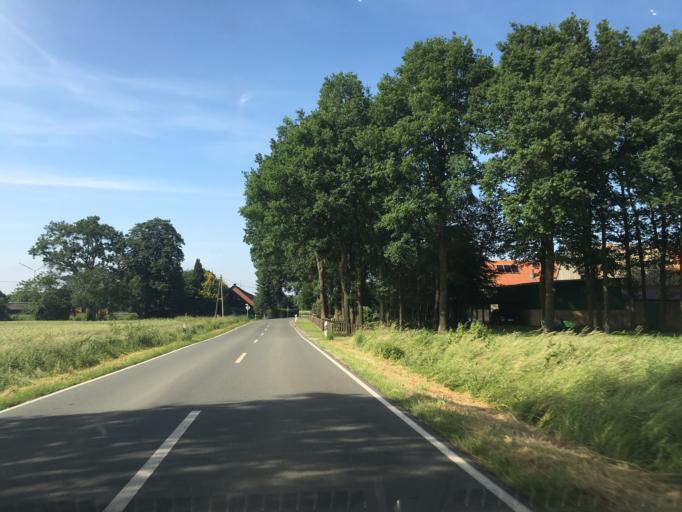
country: DE
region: North Rhine-Westphalia
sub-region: Regierungsbezirk Munster
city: Steinfurt
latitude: 52.1584
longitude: 7.3789
